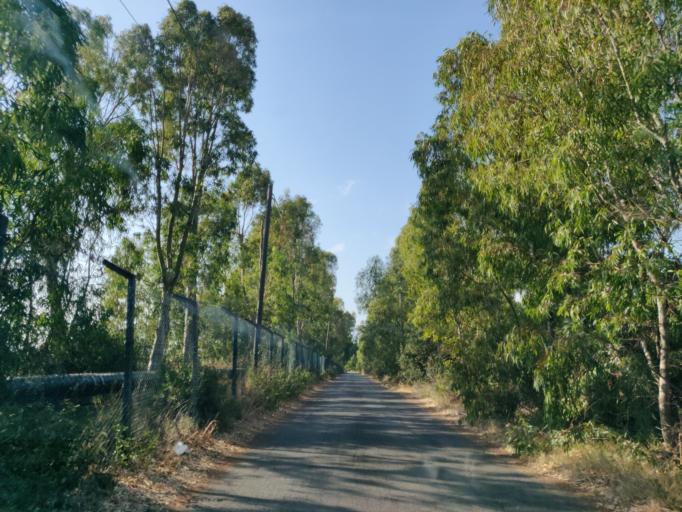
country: IT
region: Latium
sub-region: Citta metropolitana di Roma Capitale
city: Aurelia
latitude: 42.1356
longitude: 11.7613
